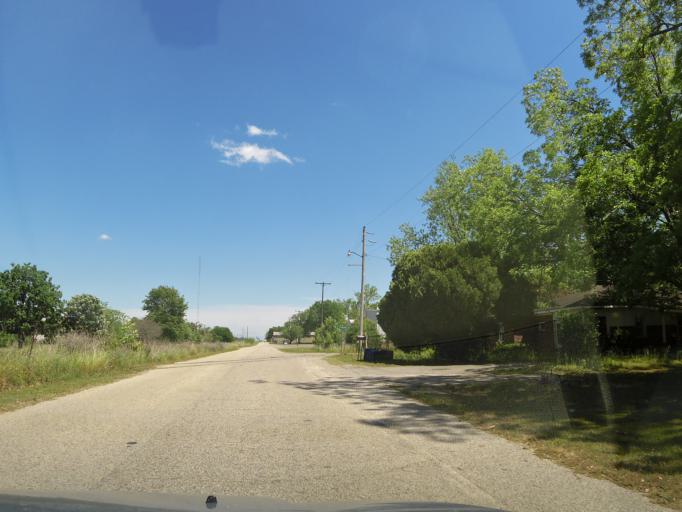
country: US
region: South Carolina
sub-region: Aiken County
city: Aiken
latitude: 33.5522
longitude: -81.7013
